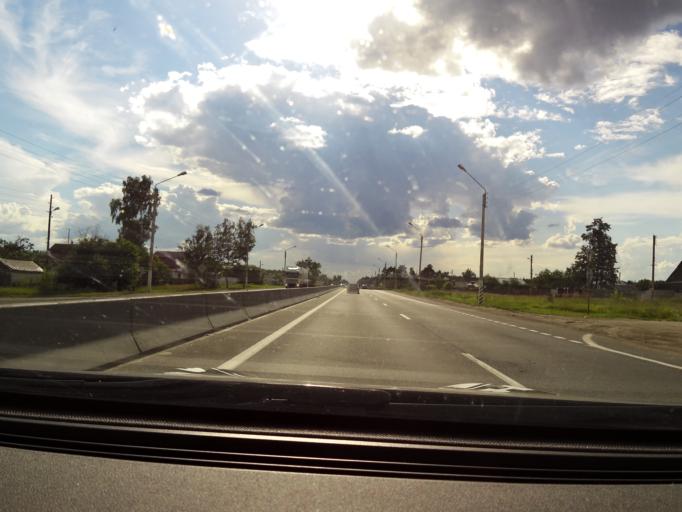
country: RU
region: Nizjnij Novgorod
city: Pyra
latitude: 56.2931
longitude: 43.3486
